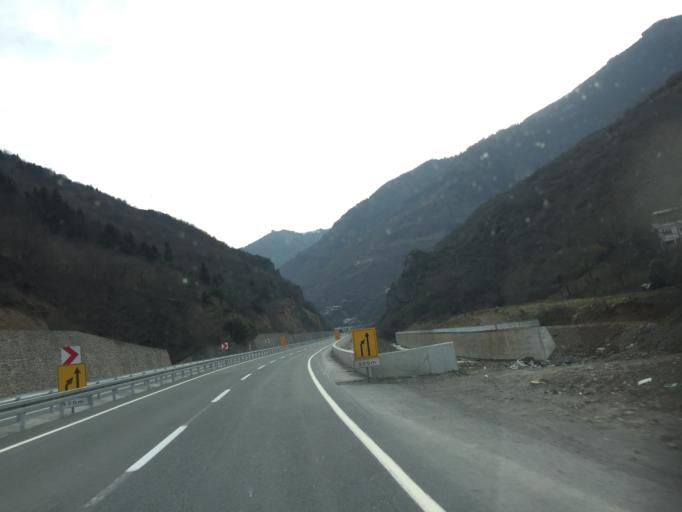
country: TR
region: Trabzon
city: Macka
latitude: 40.7859
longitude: 39.5769
